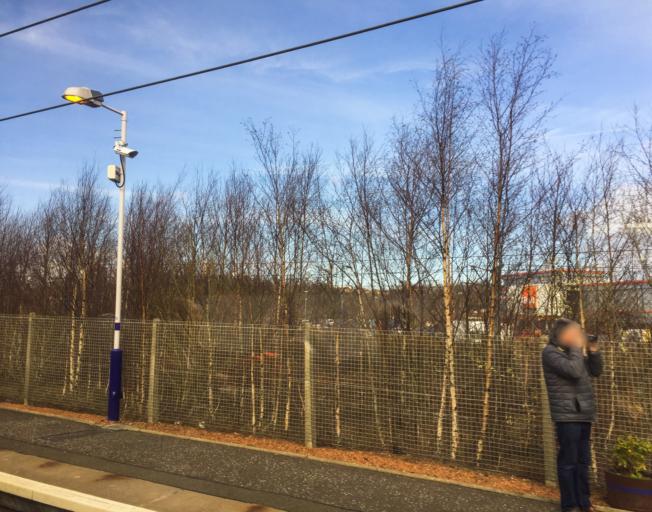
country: GB
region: Scotland
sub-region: North Lanarkshire
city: Coatbridge
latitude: 55.8540
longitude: -4.0188
